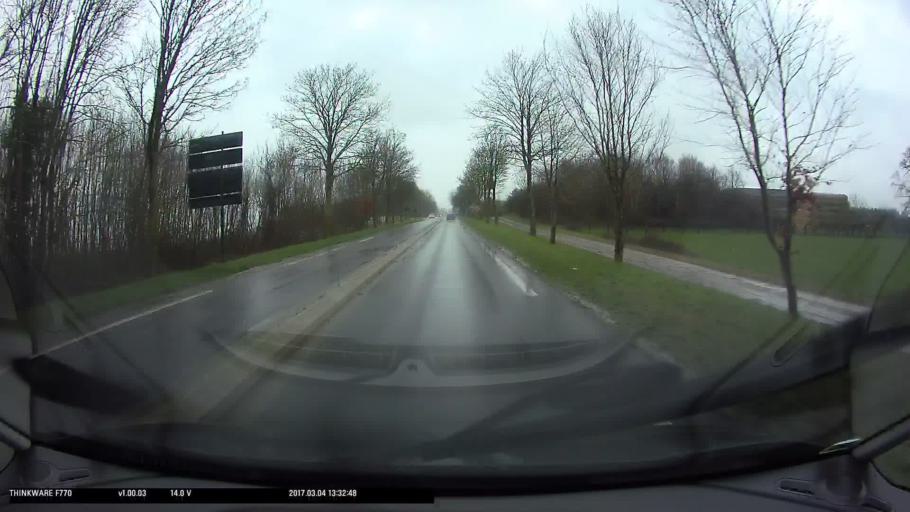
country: FR
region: Ile-de-France
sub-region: Departement du Val-d'Oise
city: Marines
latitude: 49.1293
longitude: 1.9961
